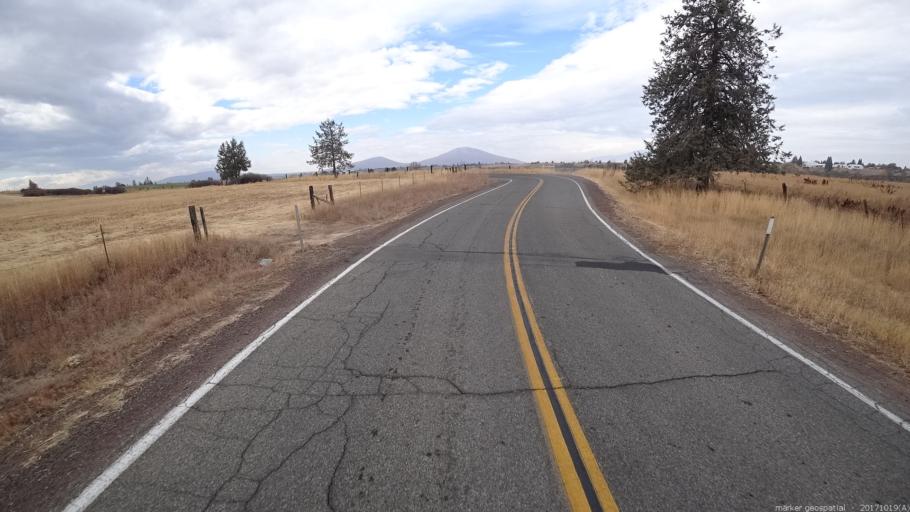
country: US
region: California
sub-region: Shasta County
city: Burney
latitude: 41.0402
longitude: -121.3883
